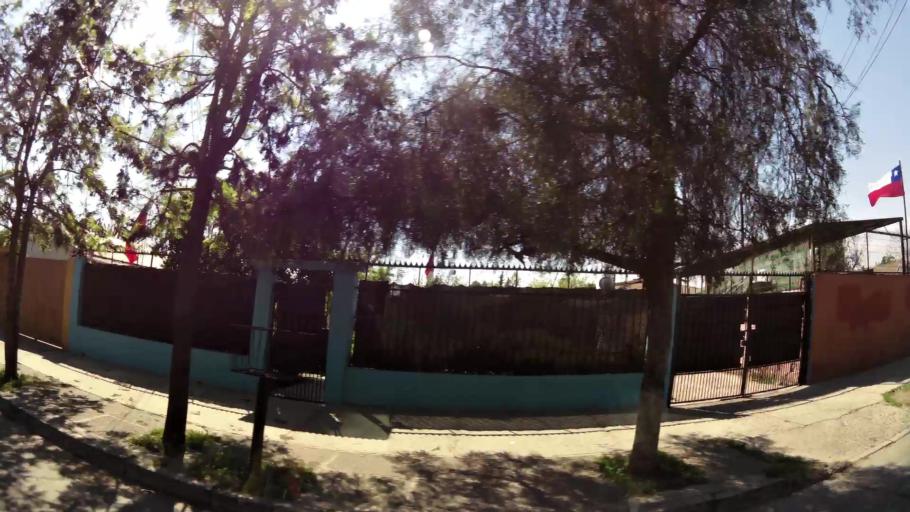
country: CL
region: Santiago Metropolitan
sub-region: Provincia de Santiago
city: La Pintana
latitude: -33.5321
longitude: -70.6394
